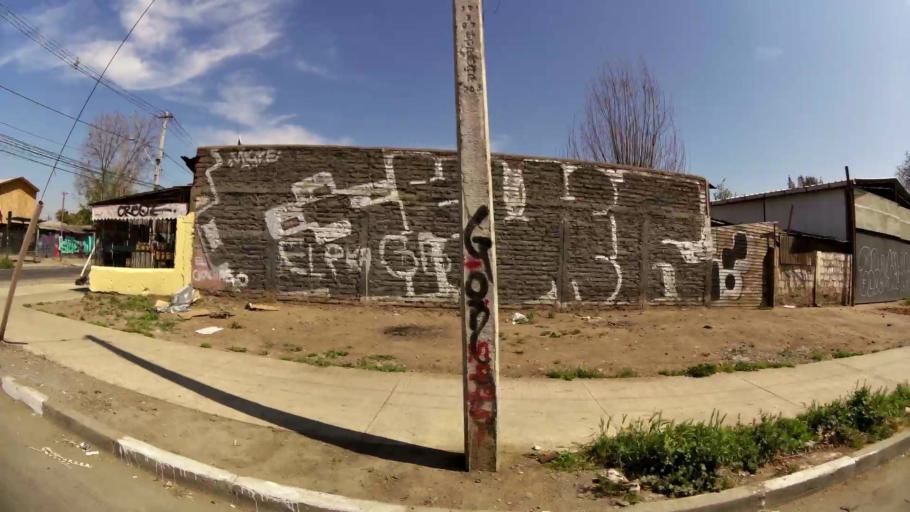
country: CL
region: Santiago Metropolitan
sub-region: Provincia de Santiago
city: Lo Prado
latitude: -33.4064
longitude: -70.7200
